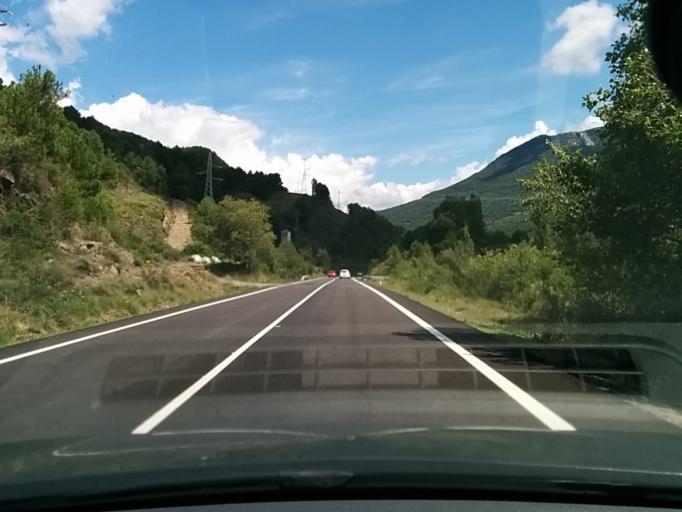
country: ES
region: Aragon
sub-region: Provincia de Huesca
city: Labuerda
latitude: 42.4703
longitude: 0.1445
